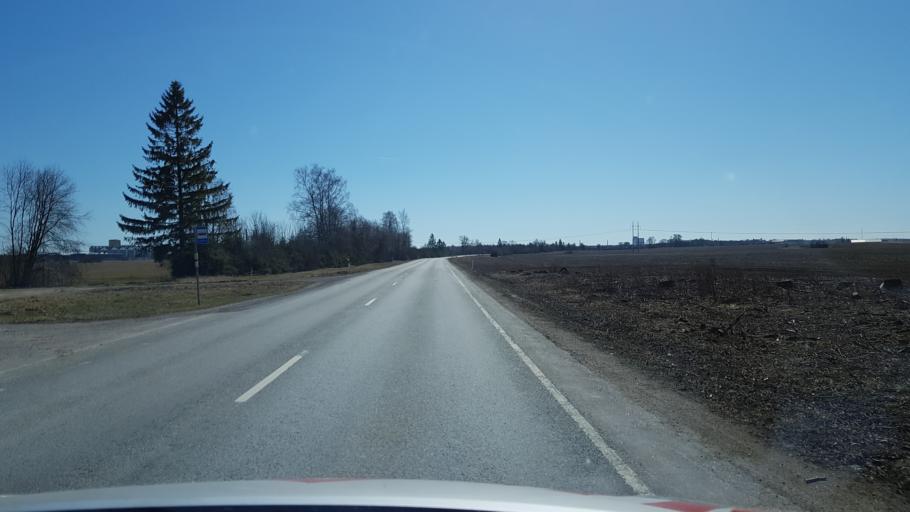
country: EE
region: Laeaene-Virumaa
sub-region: Someru vald
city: Someru
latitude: 59.3847
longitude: 26.3932
